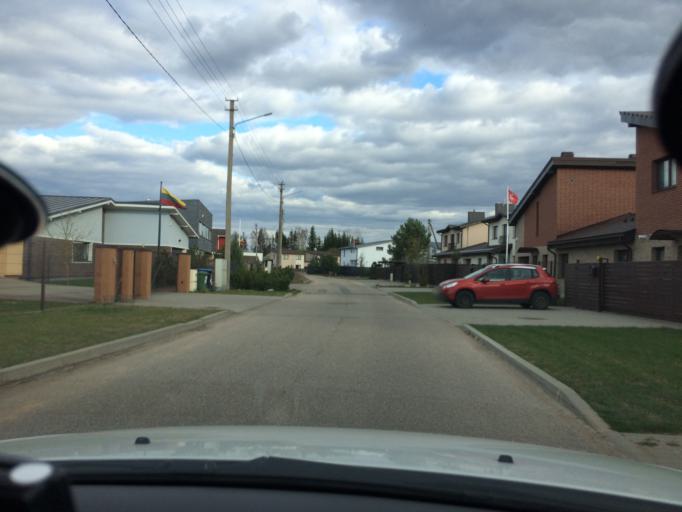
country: LT
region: Vilnius County
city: Rasos
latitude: 54.7757
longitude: 25.3471
